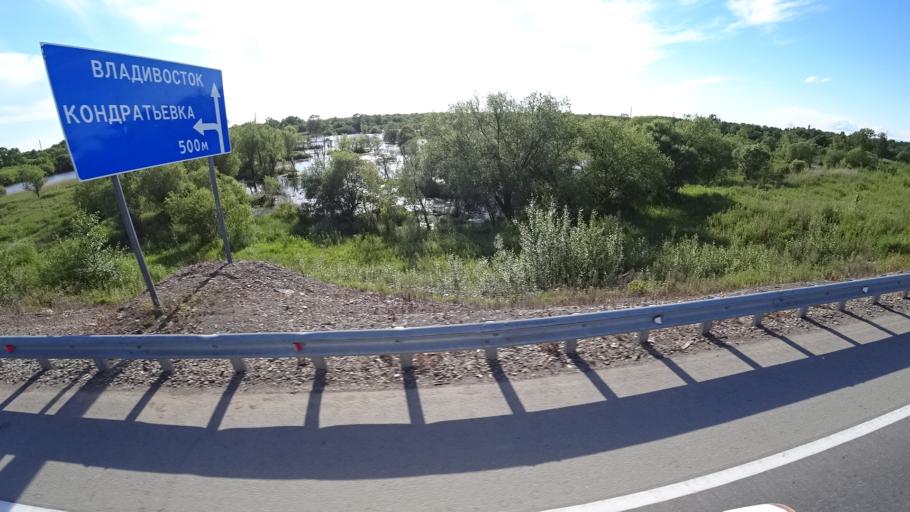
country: RU
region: Khabarovsk Krai
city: Khor
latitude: 47.8610
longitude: 134.9630
